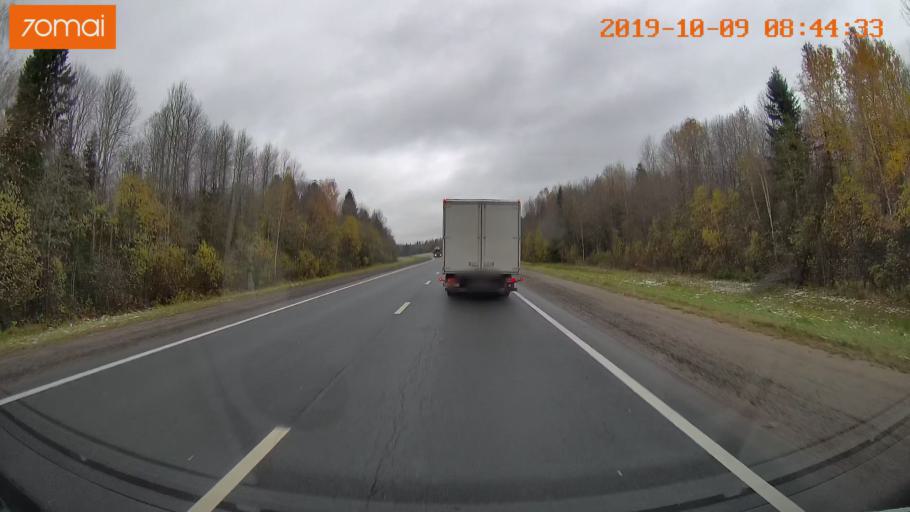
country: RU
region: Vologda
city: Gryazovets
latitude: 59.0379
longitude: 40.1068
